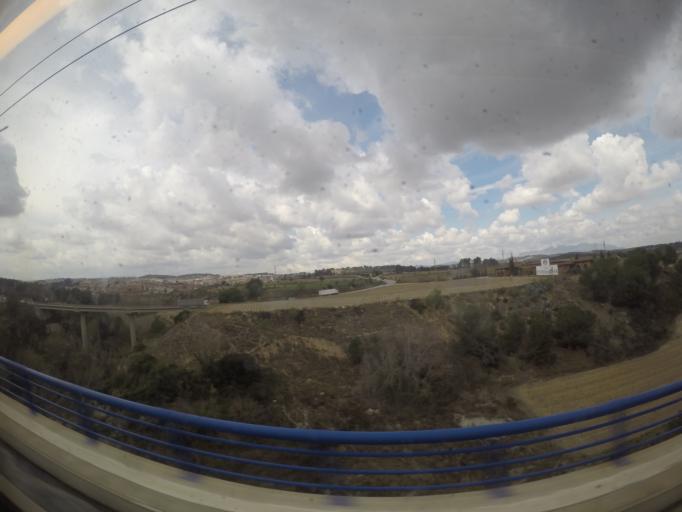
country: ES
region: Catalonia
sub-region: Provincia de Barcelona
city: Sant Sadurni d'Anoia
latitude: 41.4204
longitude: 1.7976
